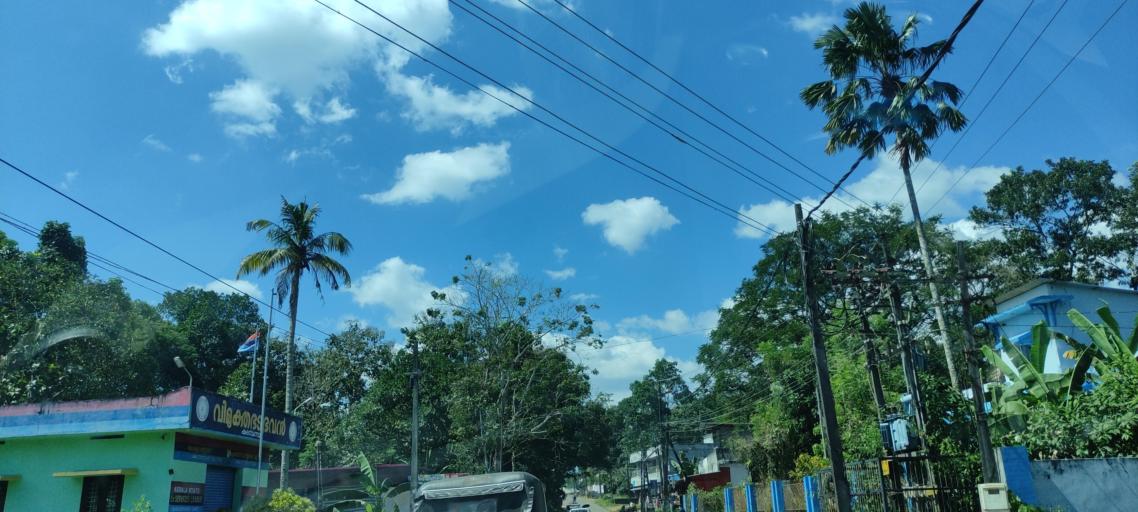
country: IN
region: Kerala
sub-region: Pattanamtitta
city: Adur
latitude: 9.0910
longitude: 76.6898
